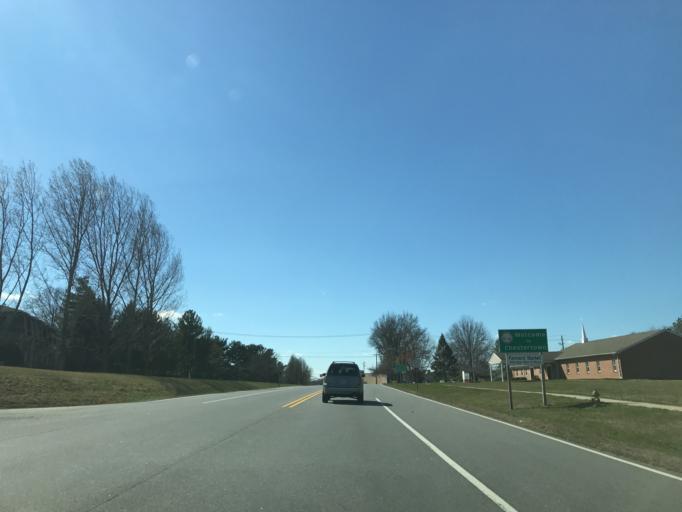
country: US
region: Maryland
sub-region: Kent County
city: Chestertown
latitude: 39.2243
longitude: -76.0645
